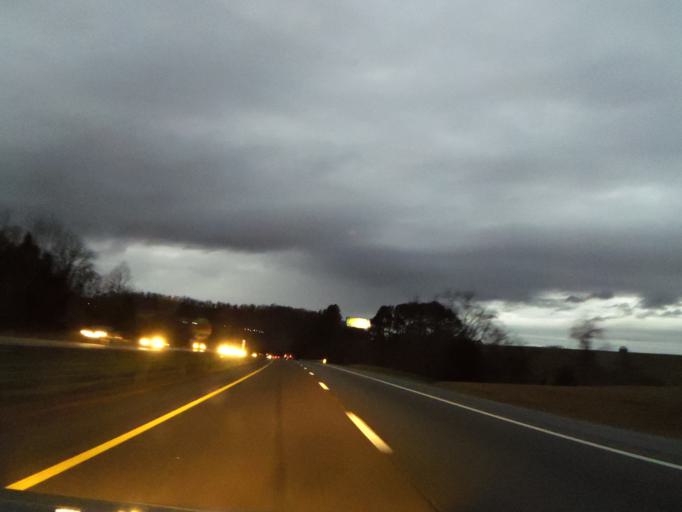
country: US
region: Tennessee
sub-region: Washington County
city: Gray
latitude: 36.4195
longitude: -82.4978
